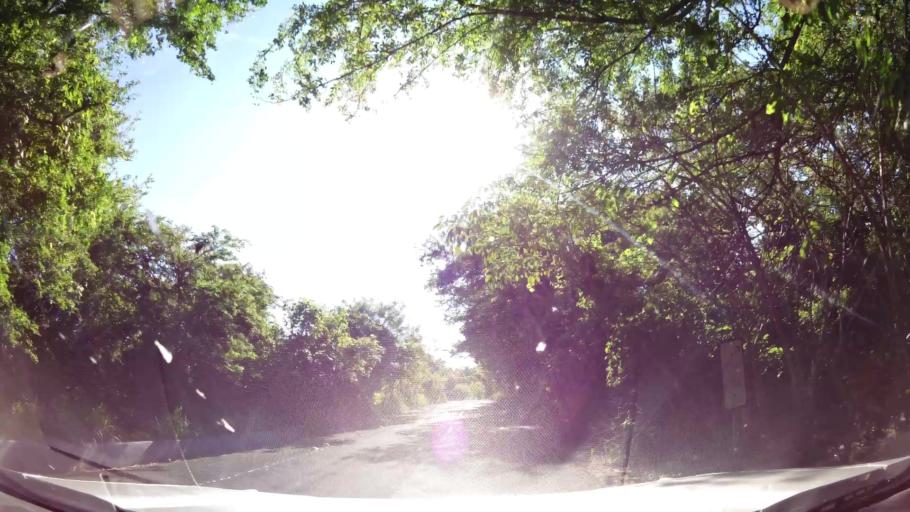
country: GT
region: Santa Rosa
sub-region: Municipio de Taxisco
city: Taxisco
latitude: 13.8906
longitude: -90.4767
